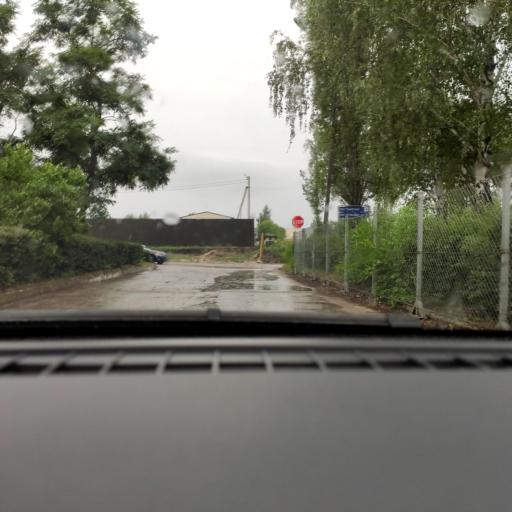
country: RU
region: Voronezj
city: Somovo
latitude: 51.7146
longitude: 39.2881
